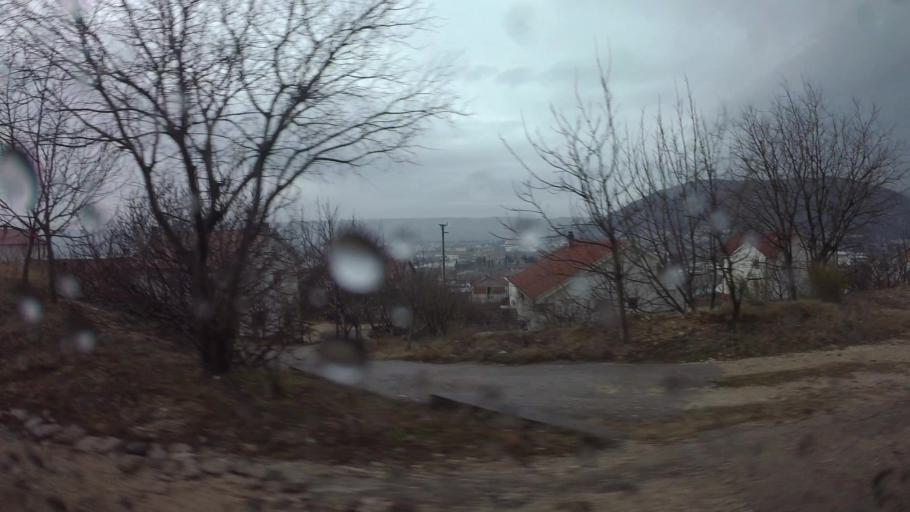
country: BA
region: Federation of Bosnia and Herzegovina
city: Rodoc
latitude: 43.3149
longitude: 17.8373
